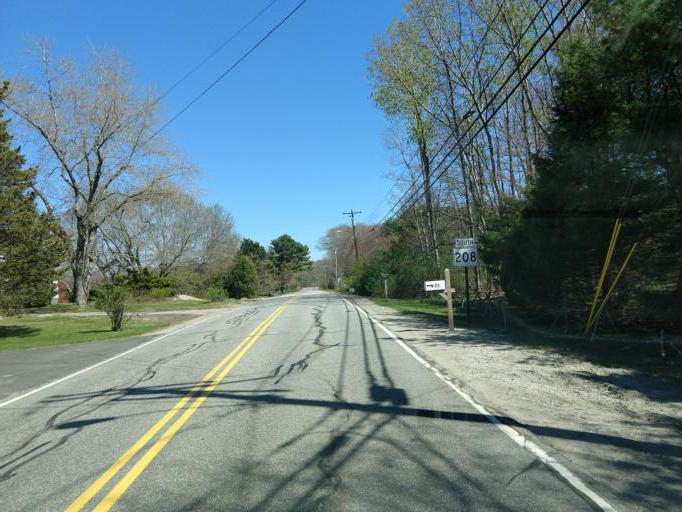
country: US
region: Maine
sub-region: York County
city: Old Orchard Beach
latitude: 43.4402
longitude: -70.3786
